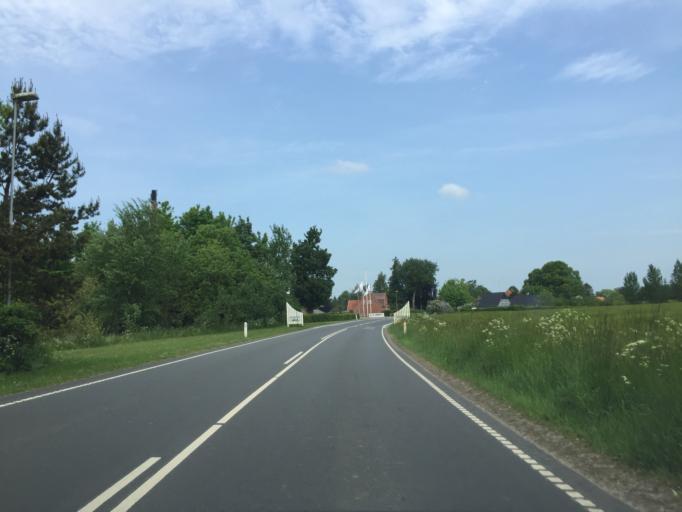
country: DK
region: South Denmark
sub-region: Svendborg Kommune
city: Thuro By
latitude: 55.1645
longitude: 10.7349
